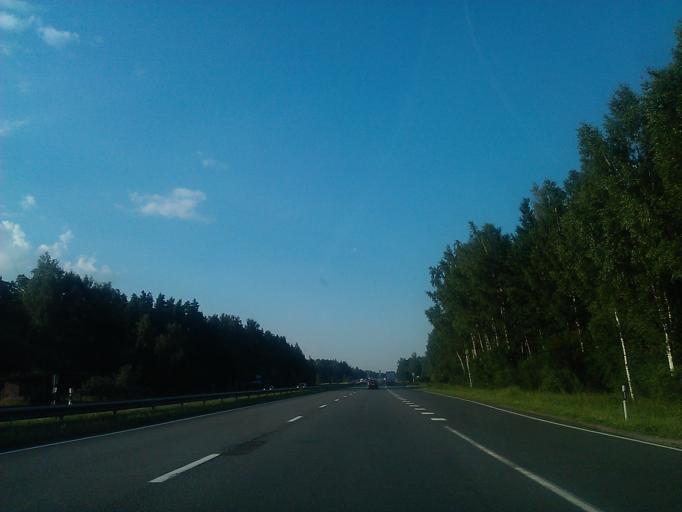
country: LV
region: Babite
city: Pinki
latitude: 56.9452
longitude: 23.9229
